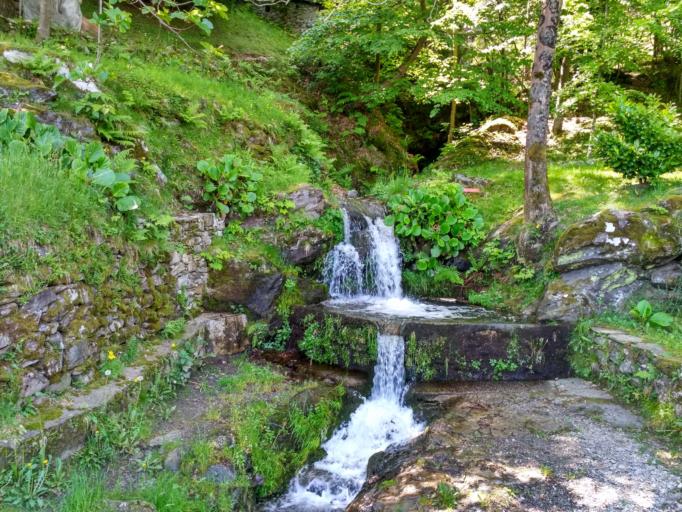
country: IT
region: Lombardy
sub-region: Provincia di Lecco
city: Sueglio
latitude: 46.1107
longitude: 9.3490
